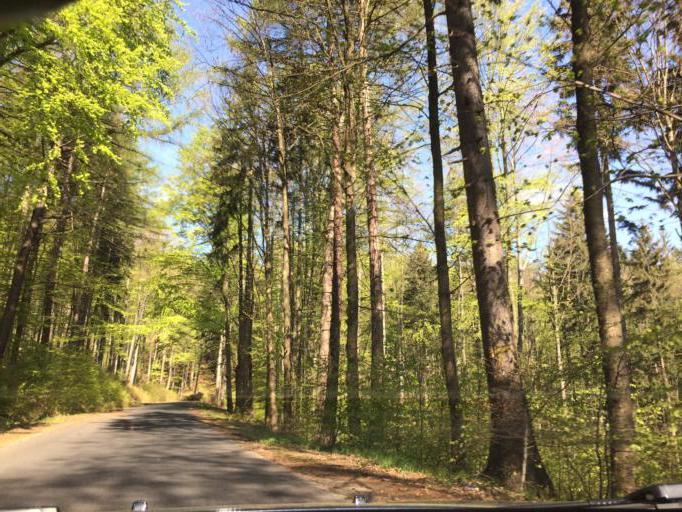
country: PL
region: Lower Silesian Voivodeship
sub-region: Powiat klodzki
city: Jugow
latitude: 50.6695
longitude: 16.5198
